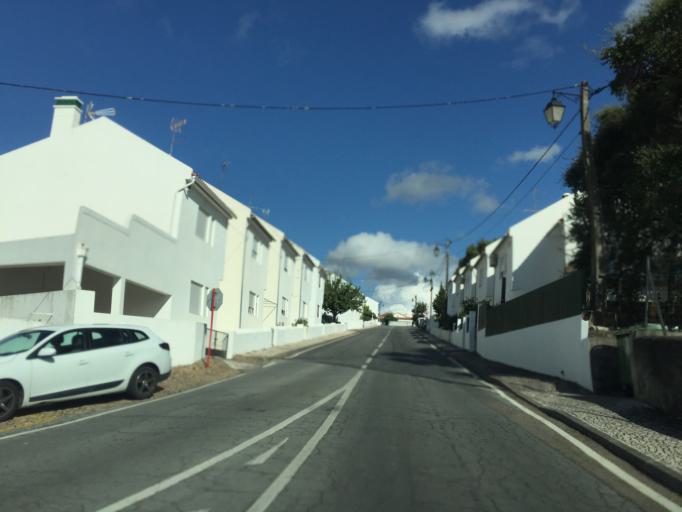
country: PT
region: Portalegre
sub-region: Marvao
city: Marvao
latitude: 39.4127
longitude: -7.3524
